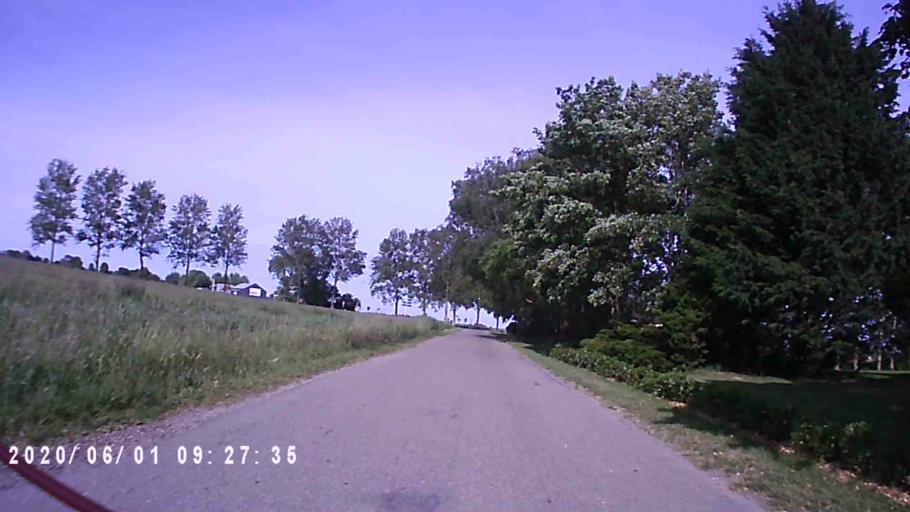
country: NL
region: Friesland
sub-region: Gemeente Leeuwarderadeel
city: Stiens
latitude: 53.2651
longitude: 5.7375
